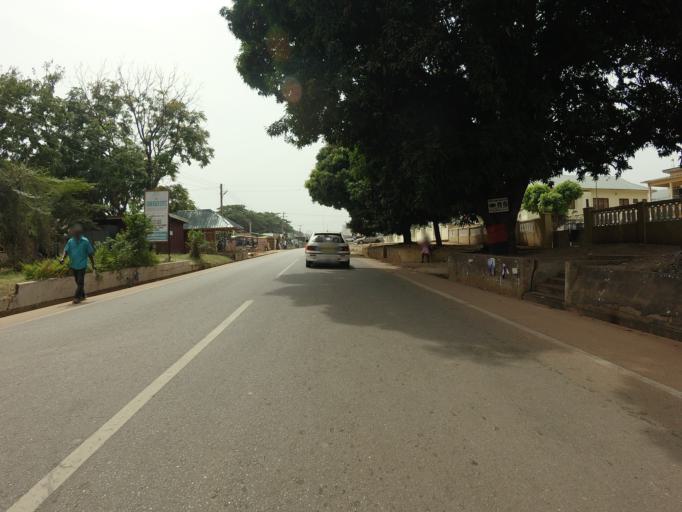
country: GH
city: Akropong
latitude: 6.0979
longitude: -0.0186
